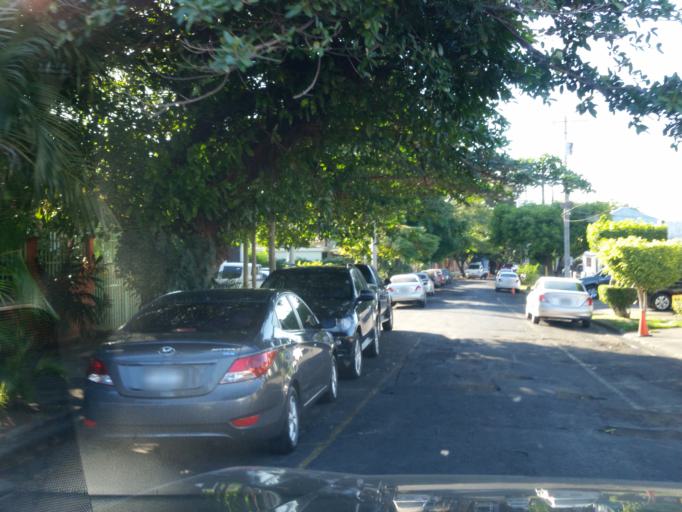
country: NI
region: Managua
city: Managua
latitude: 12.1395
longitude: -86.2772
